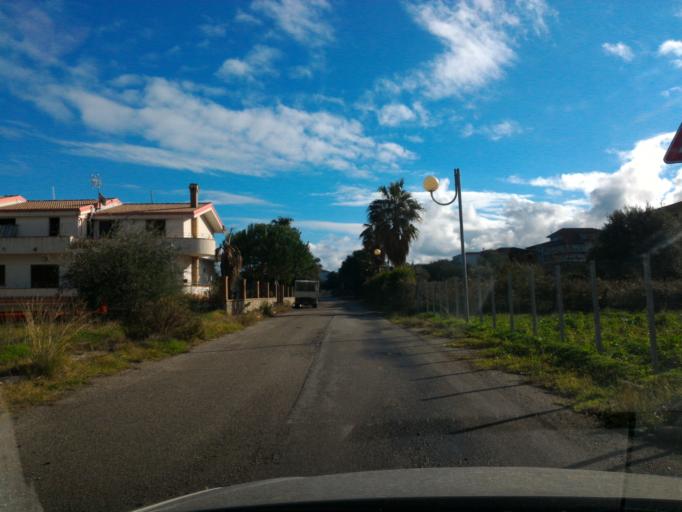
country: IT
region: Calabria
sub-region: Provincia di Crotone
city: Torretta
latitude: 39.4572
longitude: 17.0343
